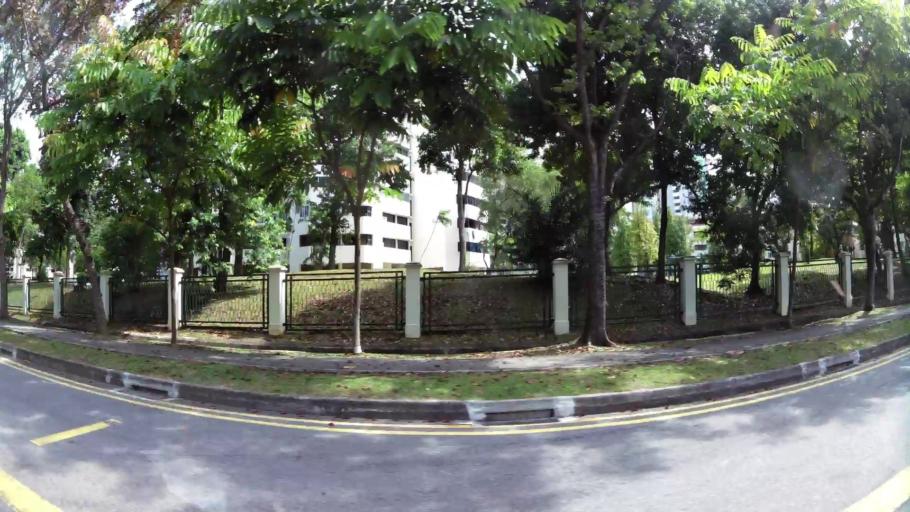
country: SG
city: Singapore
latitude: 1.3372
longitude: 103.7345
